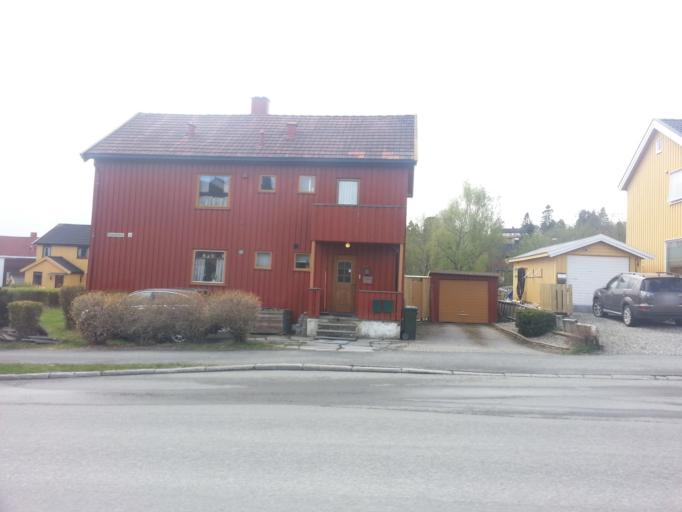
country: NO
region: Sor-Trondelag
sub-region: Trondheim
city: Trondheim
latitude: 63.4158
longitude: 10.3627
